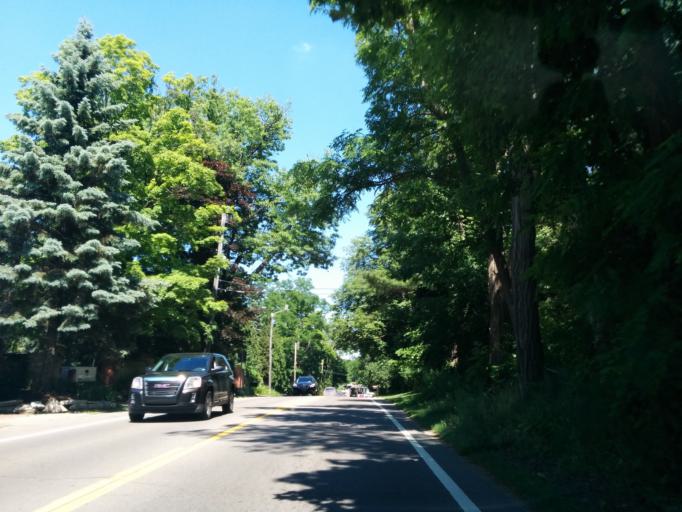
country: US
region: Michigan
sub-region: Oakland County
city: Orchard Lake
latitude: 42.5775
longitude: -83.3658
